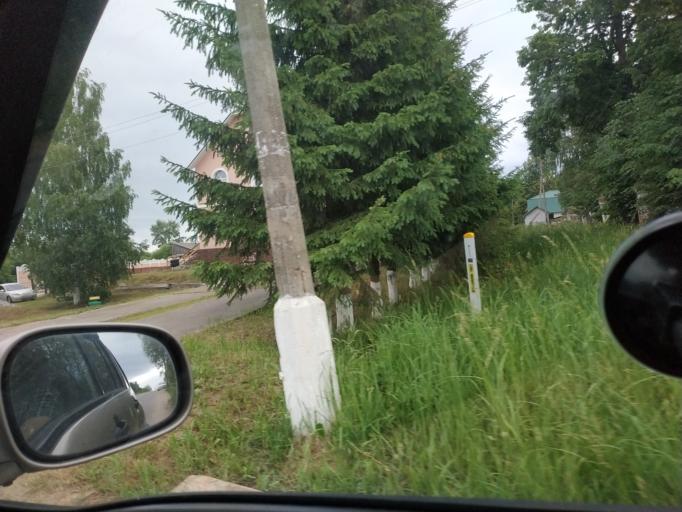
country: RU
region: Moskovskaya
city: Krasnoarmeysk
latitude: 56.0872
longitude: 38.2255
